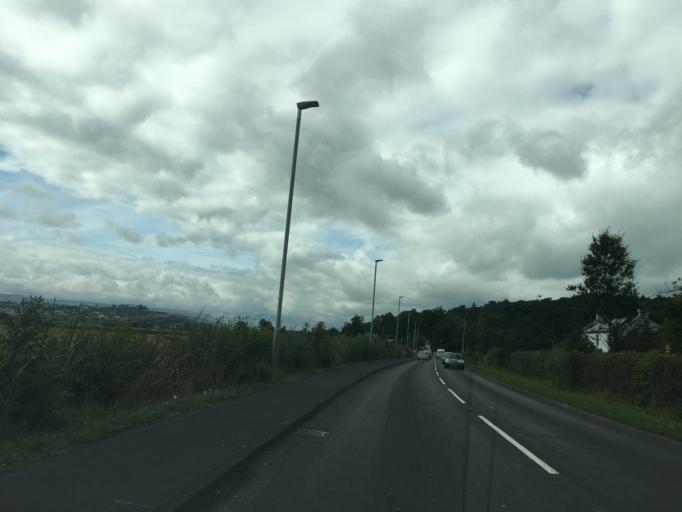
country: GB
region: Scotland
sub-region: Stirling
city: Stirling
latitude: 56.1335
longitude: -3.9017
